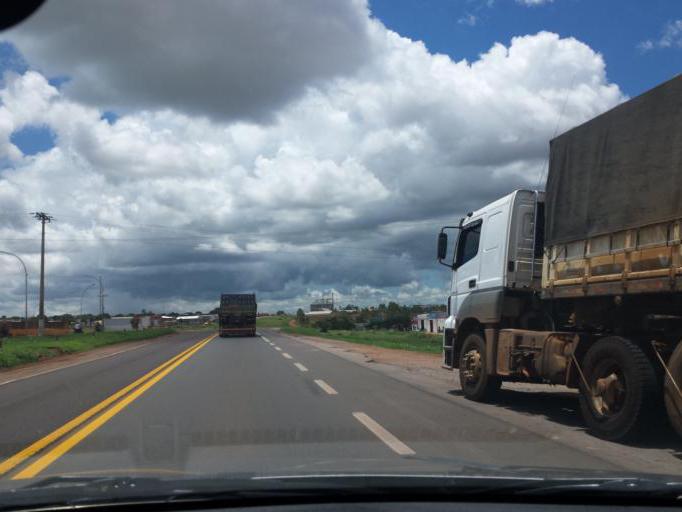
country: BR
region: Goias
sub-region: Cristalina
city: Cristalina
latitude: -16.7688
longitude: -47.6180
